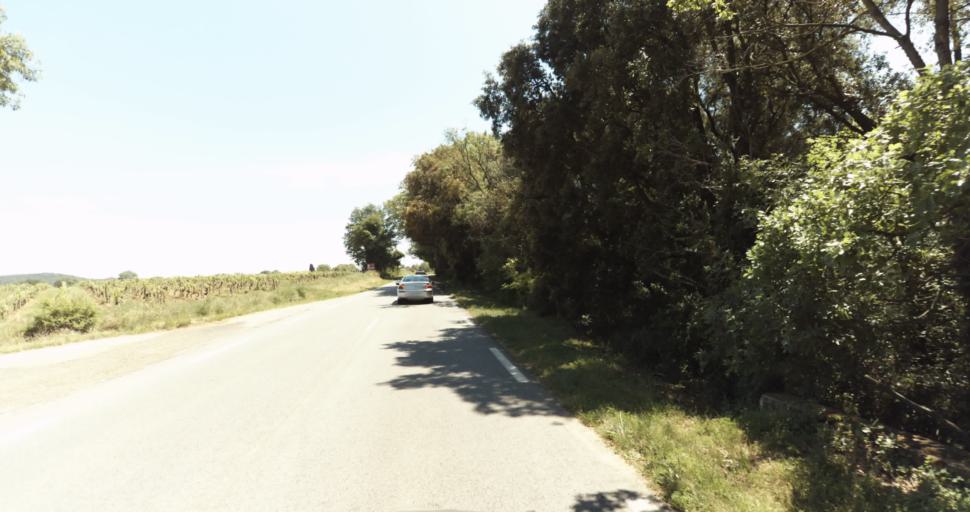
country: FR
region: Provence-Alpes-Cote d'Azur
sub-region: Departement du Var
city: Hyeres
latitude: 43.1487
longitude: 6.1487
